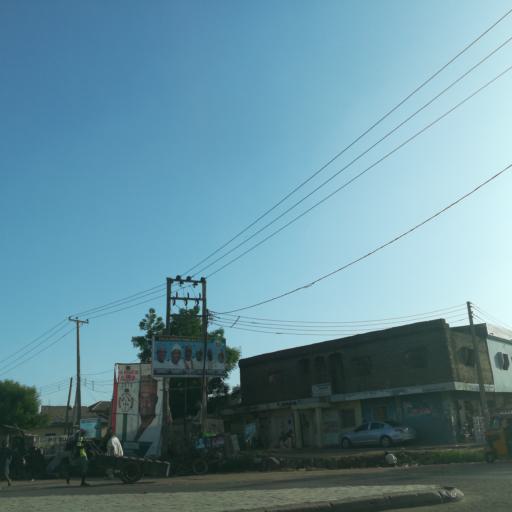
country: NG
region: Kano
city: Kano
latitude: 12.0153
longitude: 8.5052
